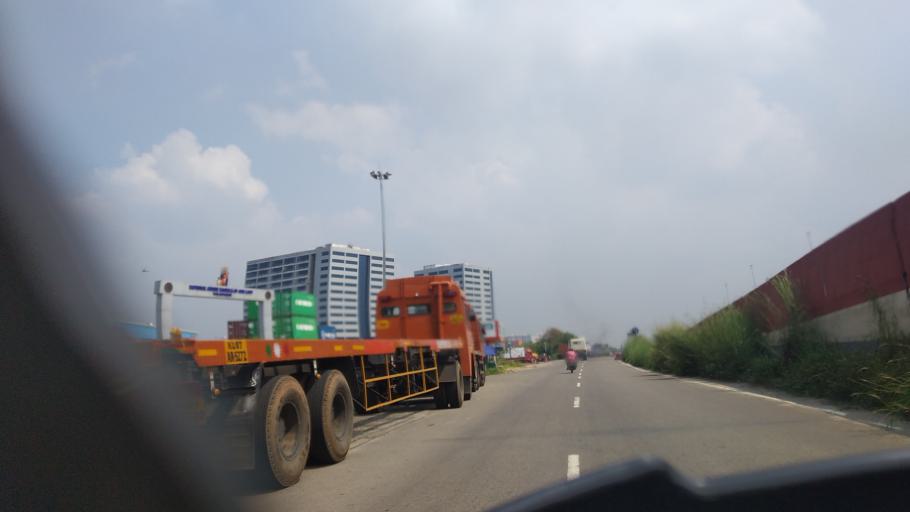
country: IN
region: Kerala
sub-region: Ernakulam
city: Cochin
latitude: 9.9856
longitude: 76.2499
